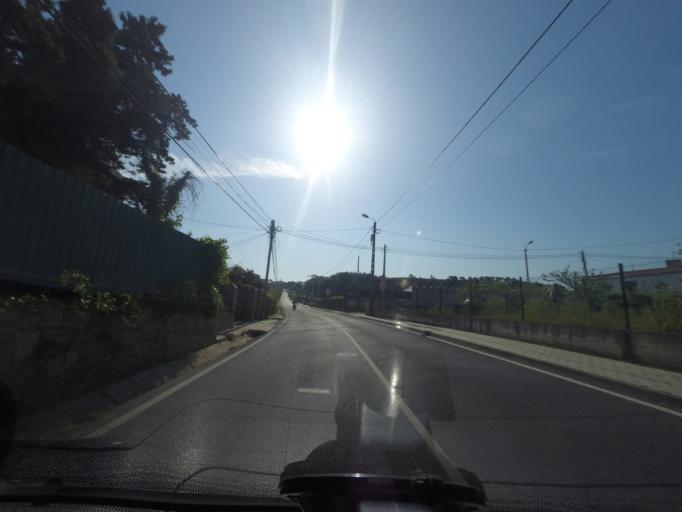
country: PT
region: Lisbon
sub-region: Cascais
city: Alcabideche
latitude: 38.7513
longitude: -9.4445
